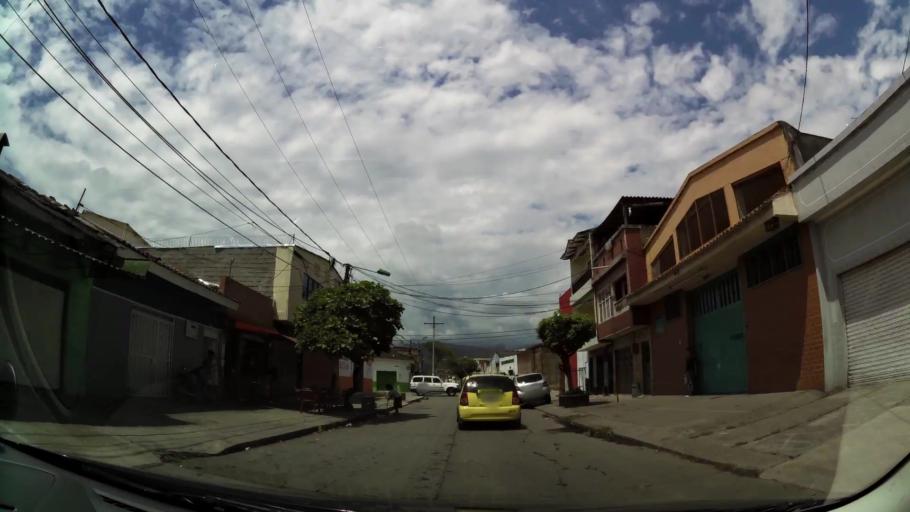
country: CO
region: Valle del Cauca
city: Cali
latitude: 3.4488
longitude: -76.5214
